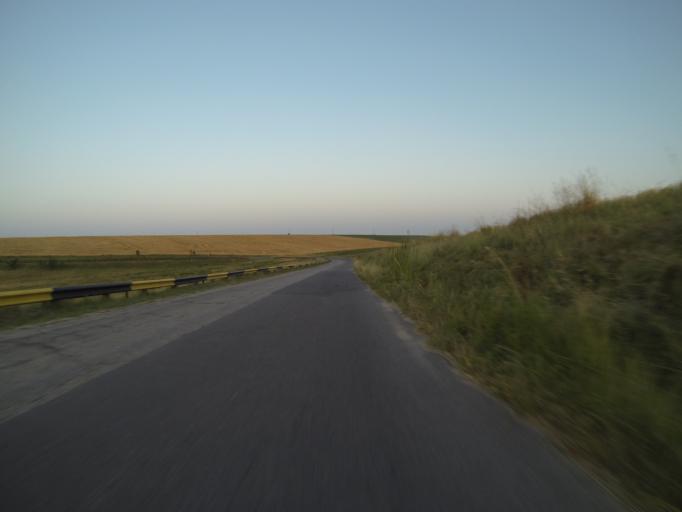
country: RO
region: Dolj
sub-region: Comuna Dranicu
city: Padea
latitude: 44.0102
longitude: 23.8712
